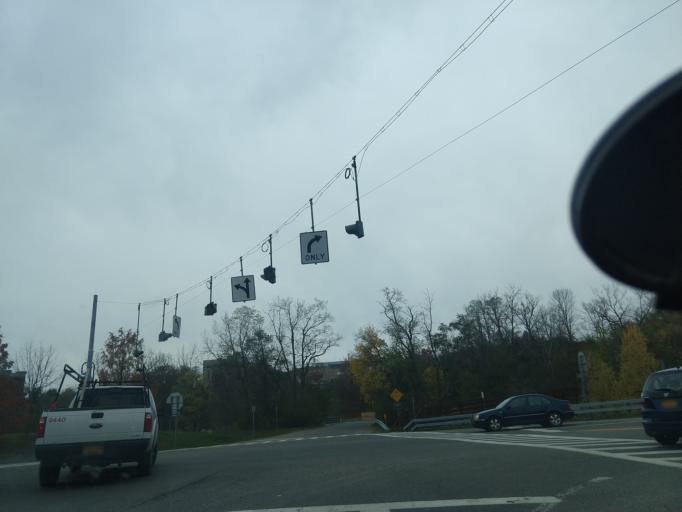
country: US
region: New York
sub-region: Tompkins County
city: East Ithaca
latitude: 42.4436
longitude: -76.4703
